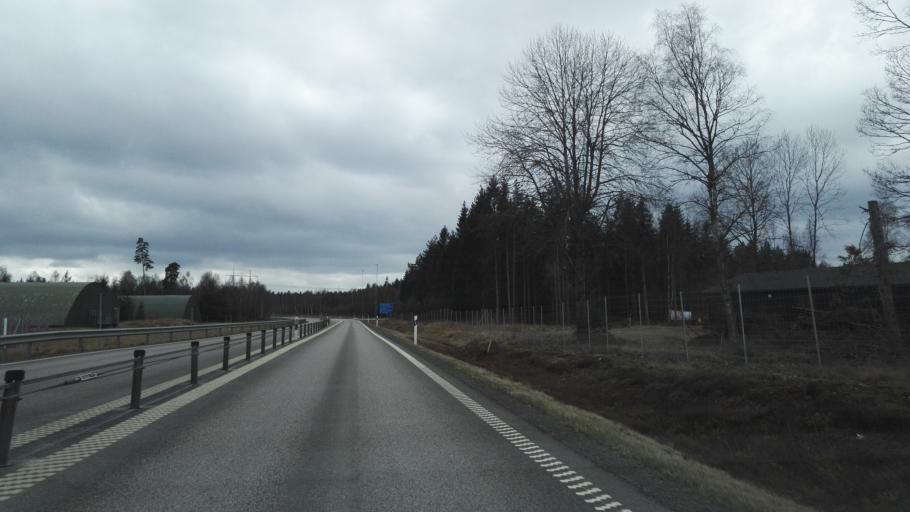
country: SE
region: Kronoberg
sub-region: Almhults Kommun
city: AElmhult
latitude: 56.6618
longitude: 14.2962
